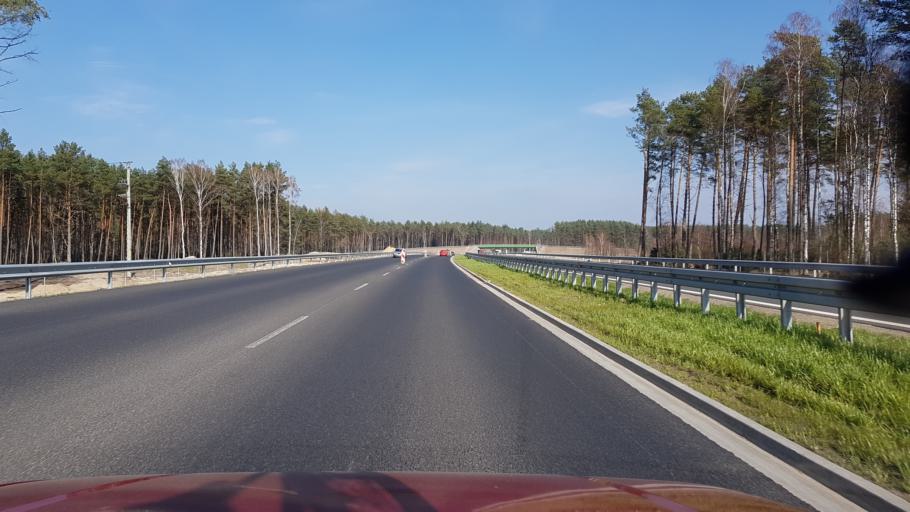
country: PL
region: West Pomeranian Voivodeship
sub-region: Powiat goleniowski
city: Mosty
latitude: 53.6093
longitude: 14.9005
